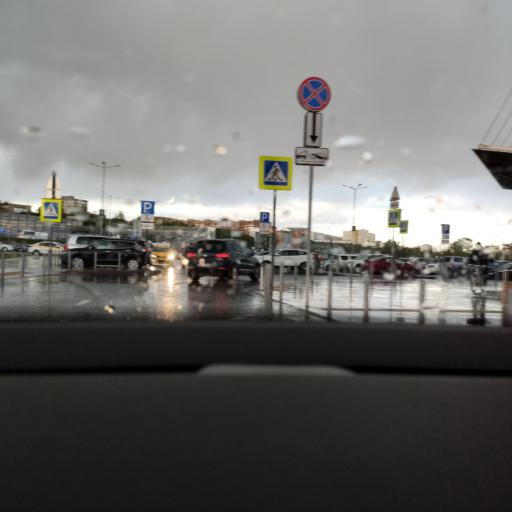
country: RU
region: Moskovskaya
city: Balashikha
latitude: 55.7931
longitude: 37.9440
